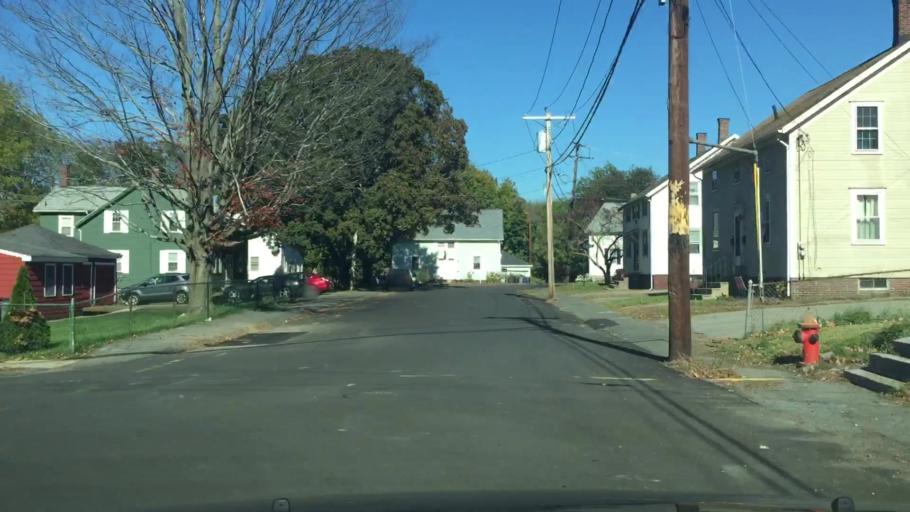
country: US
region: Massachusetts
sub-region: Essex County
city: North Andover
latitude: 42.6995
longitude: -71.1220
